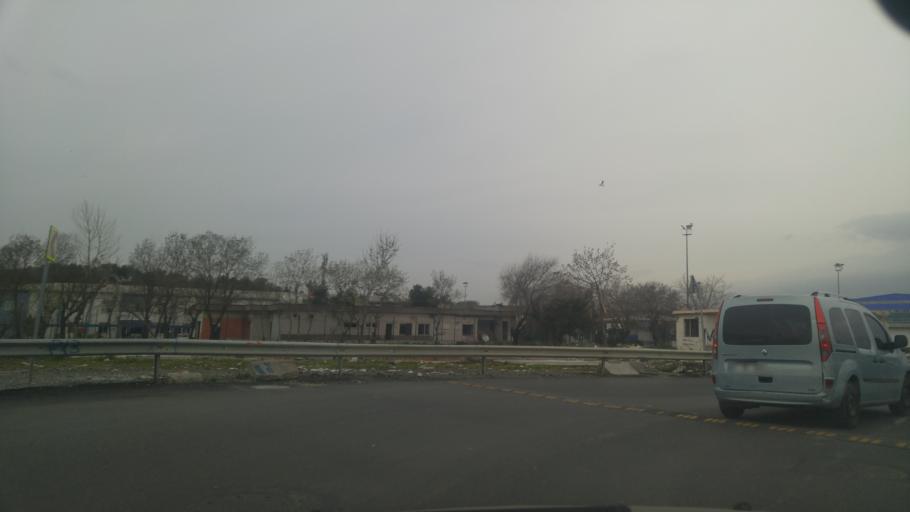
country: TR
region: Istanbul
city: Mahmutbey
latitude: 41.0114
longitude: 28.7660
